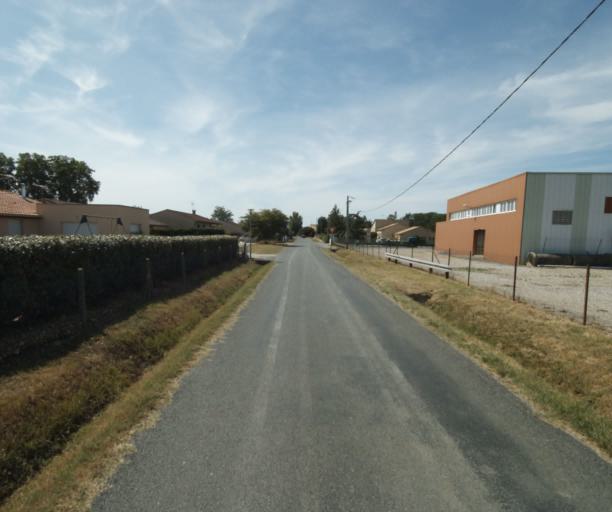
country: FR
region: Midi-Pyrenees
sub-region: Departement du Tarn
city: Puylaurens
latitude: 43.5197
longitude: 2.0115
